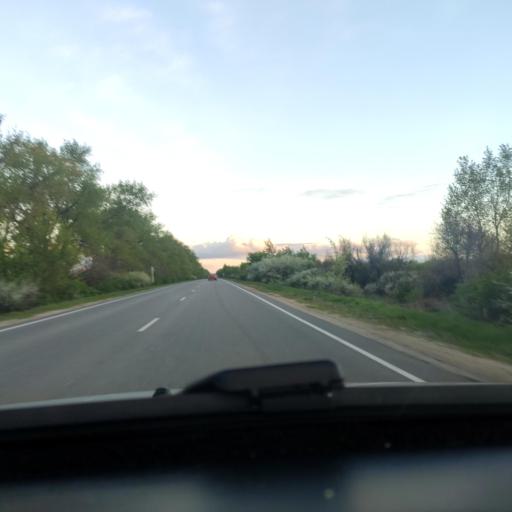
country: RU
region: Voronezj
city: Novovoronezh
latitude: 51.3968
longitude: 39.2979
